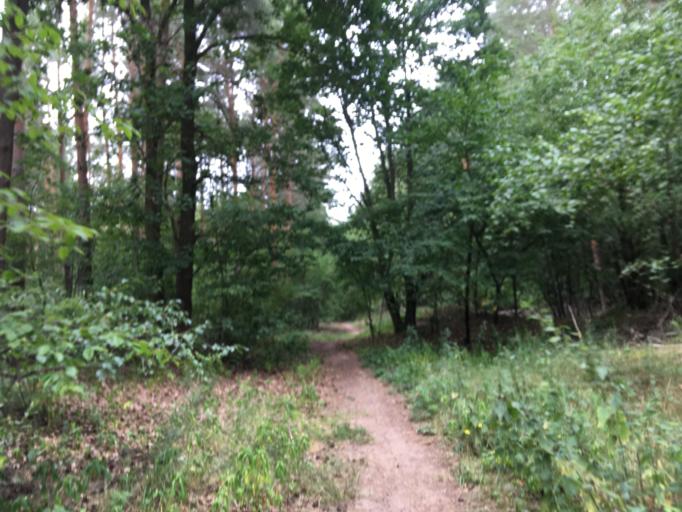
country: DE
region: Brandenburg
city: Bernau bei Berlin
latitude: 52.6436
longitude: 13.5924
